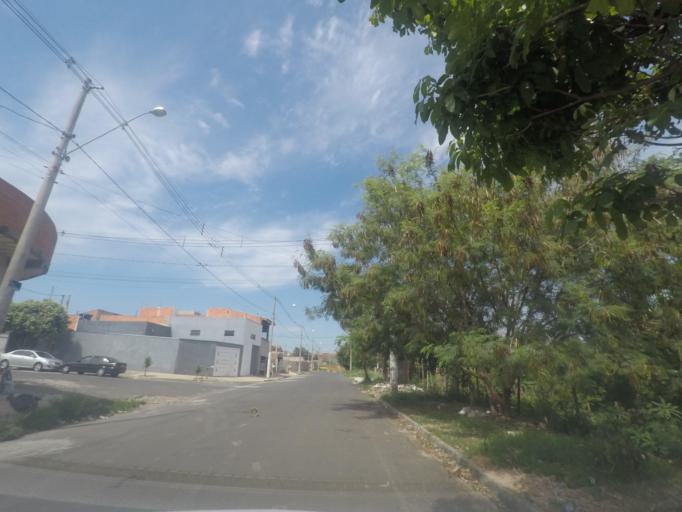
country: BR
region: Sao Paulo
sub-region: Sumare
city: Sumare
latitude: -22.7996
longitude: -47.2622
